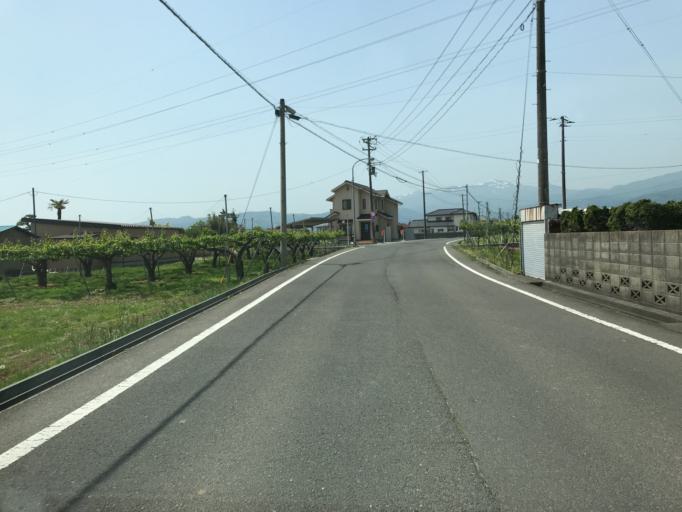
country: JP
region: Fukushima
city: Fukushima-shi
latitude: 37.7617
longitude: 140.4157
